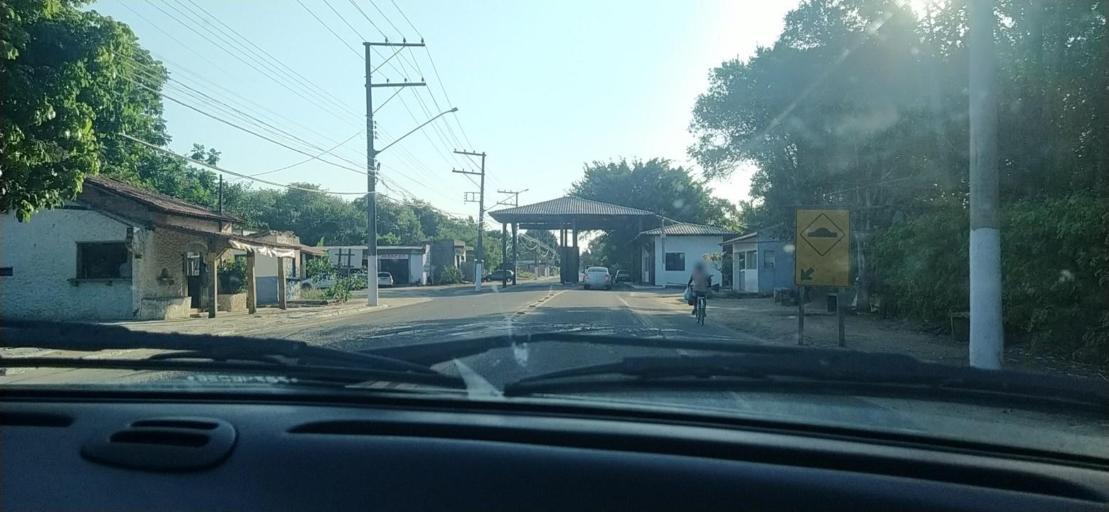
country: BR
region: Espirito Santo
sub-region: Conceicao Da Barra
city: Conceicao da Barra
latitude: -18.5674
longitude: -39.7471
